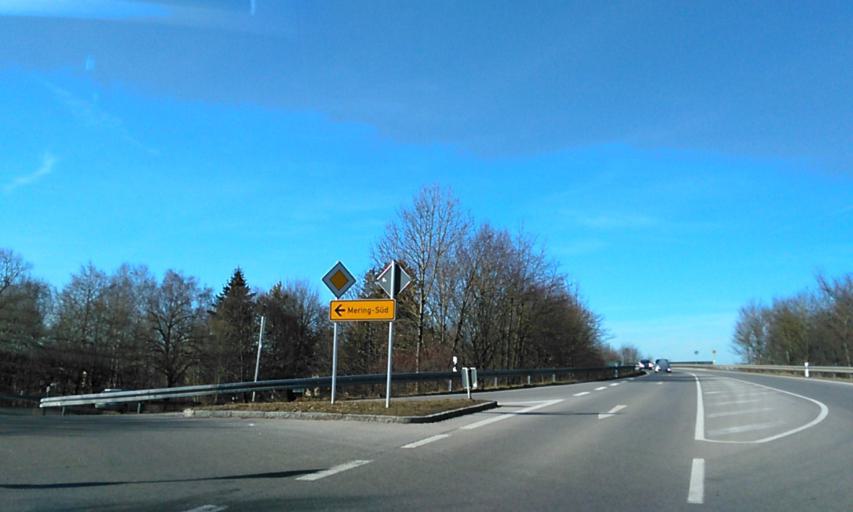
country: DE
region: Bavaria
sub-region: Swabia
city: Merching
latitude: 48.2527
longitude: 10.9873
